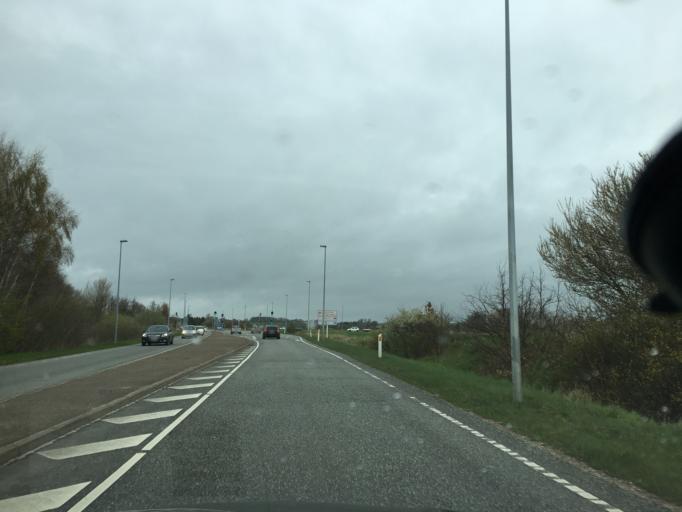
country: DK
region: Zealand
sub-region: Odsherred Kommune
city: Hojby
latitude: 55.8963
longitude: 11.5682
